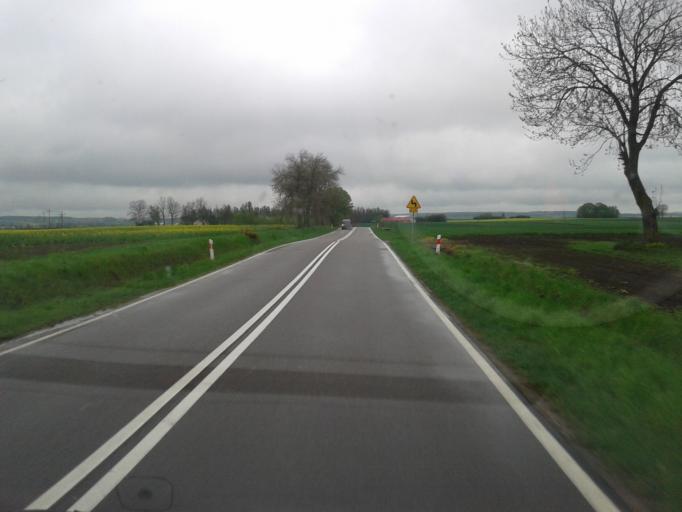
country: PL
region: Lublin Voivodeship
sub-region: Powiat tomaszowski
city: Telatyn
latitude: 50.5456
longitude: 23.9270
